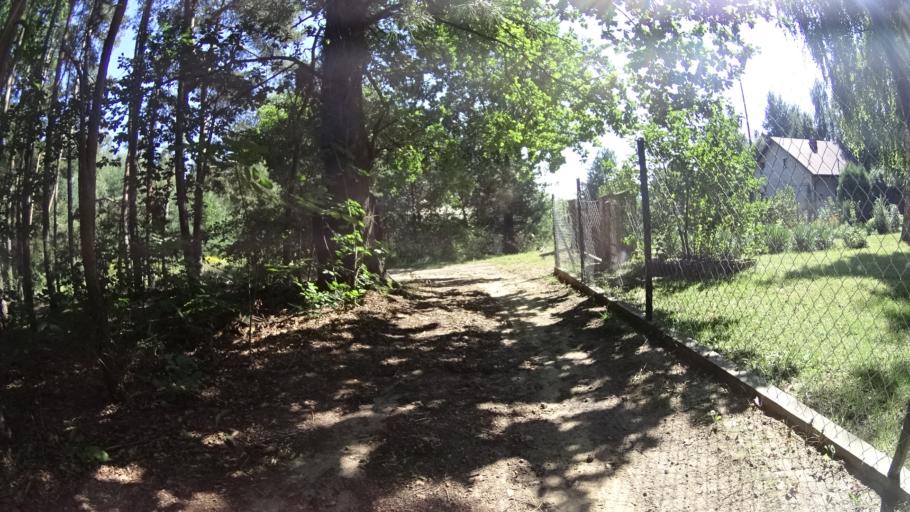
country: PL
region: Masovian Voivodeship
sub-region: Powiat bialobrzeski
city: Bialobrzegi
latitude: 51.6683
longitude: 20.9248
